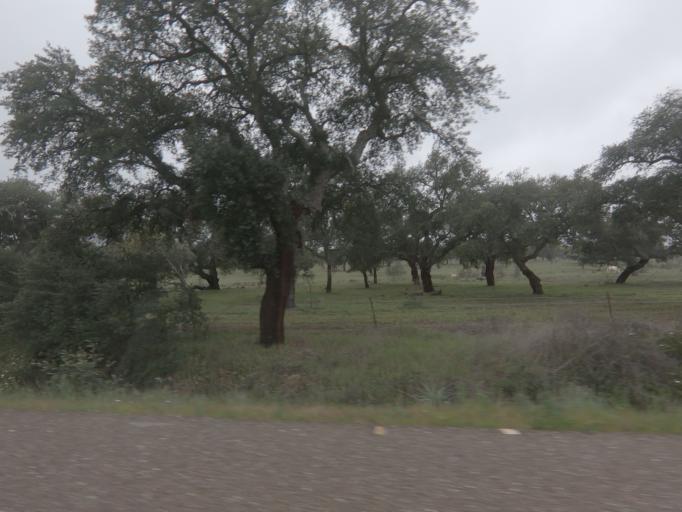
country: ES
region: Extremadura
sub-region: Provincia de Badajoz
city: Puebla de Obando
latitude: 39.1962
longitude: -6.5944
